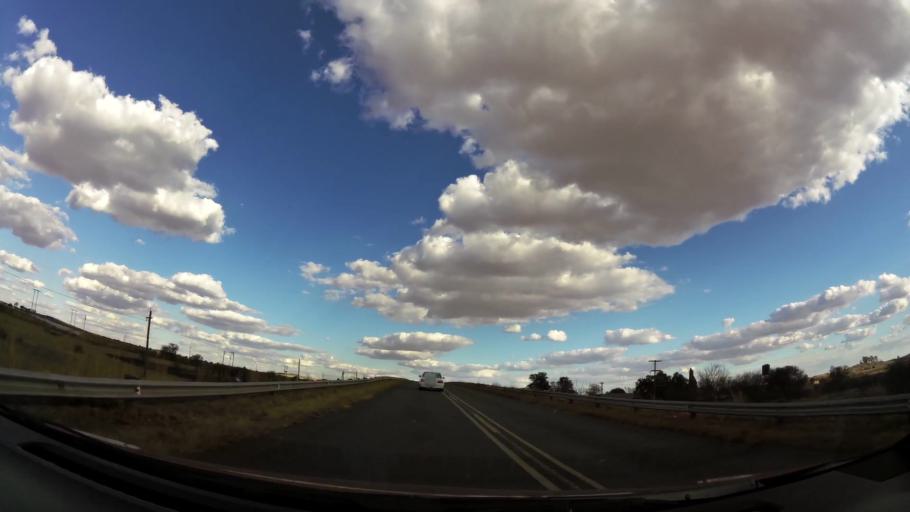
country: ZA
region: North-West
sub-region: Dr Kenneth Kaunda District Municipality
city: Potchefstroom
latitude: -26.6181
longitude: 27.1099
